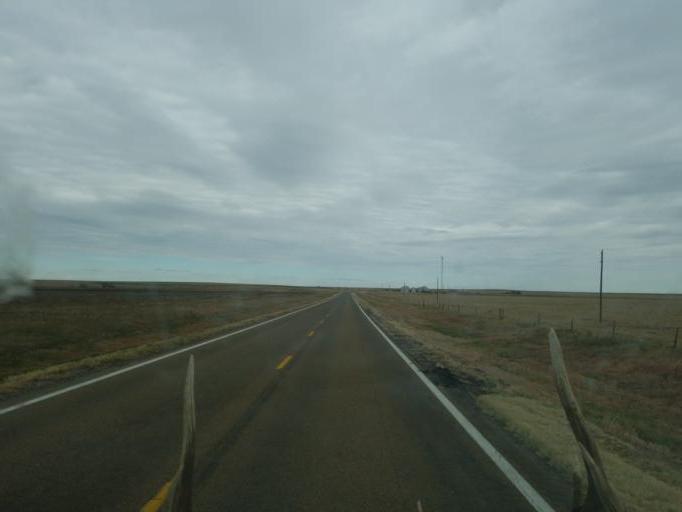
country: US
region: Kansas
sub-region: Wallace County
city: Sharon Springs
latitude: 38.9599
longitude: -101.4682
